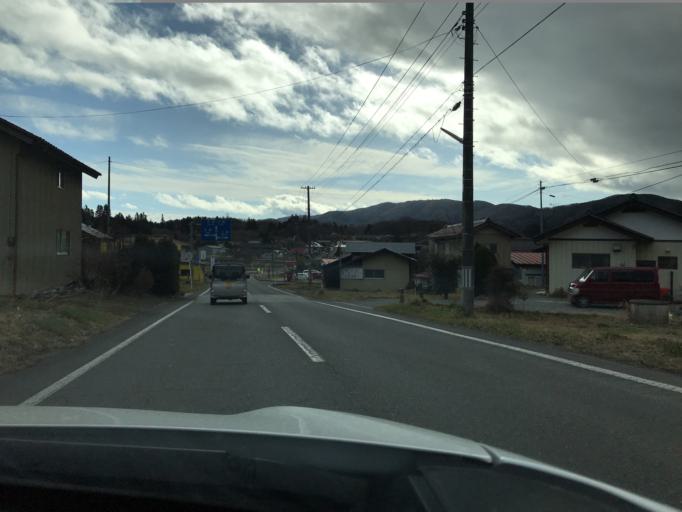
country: JP
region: Fukushima
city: Funehikimachi-funehiki
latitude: 37.3959
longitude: 140.5920
